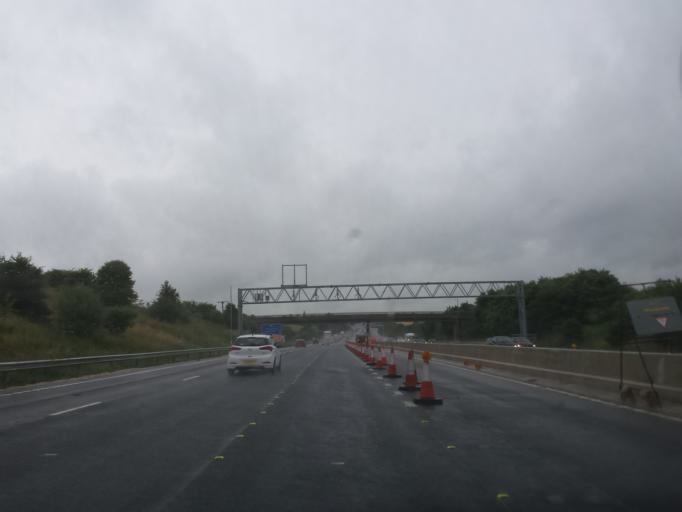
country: GB
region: England
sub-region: Rotherham
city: Wales
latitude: 53.3533
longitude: -1.2860
